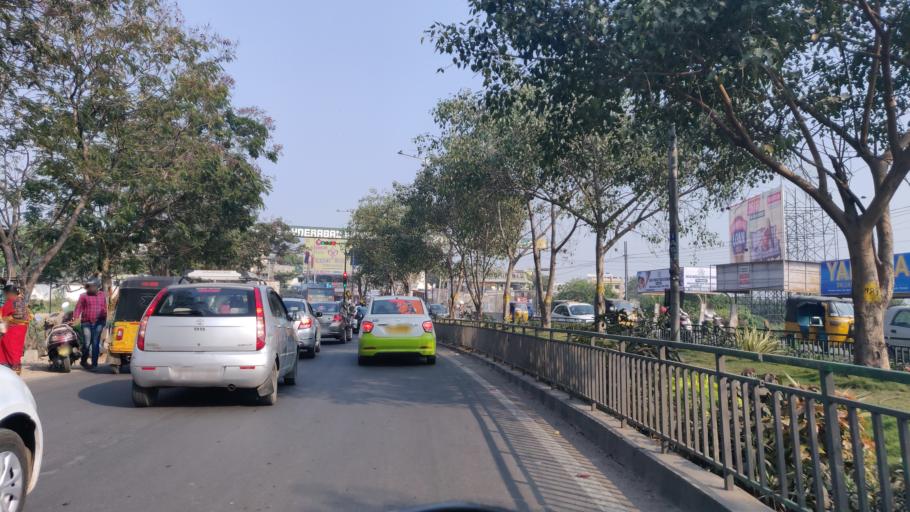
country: IN
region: Telangana
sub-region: Rangareddi
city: Uppal Kalan
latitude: 17.4012
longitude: 78.5807
